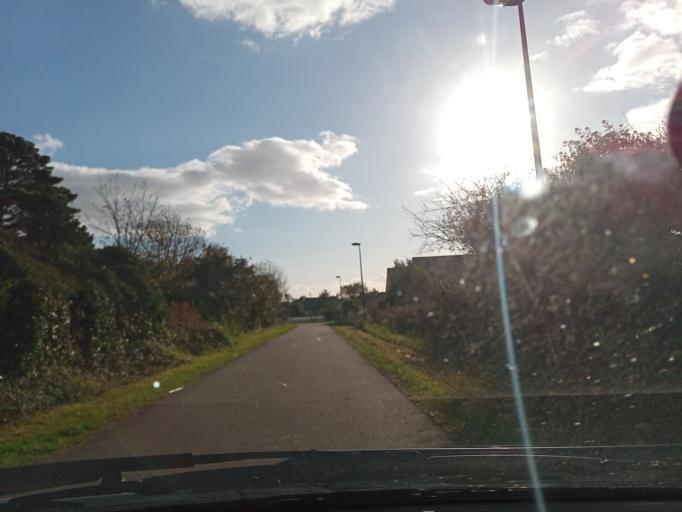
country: FR
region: Brittany
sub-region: Departement du Finistere
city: Audierne
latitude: 48.0208
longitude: -4.5135
